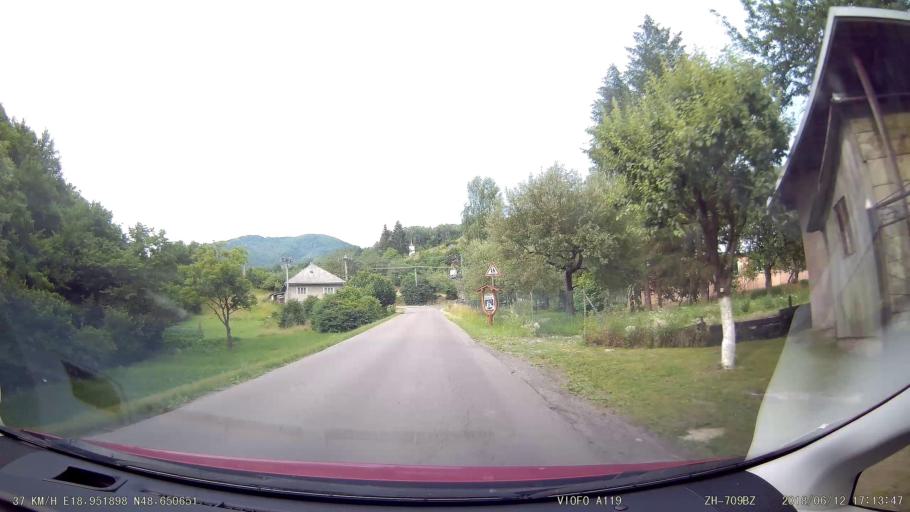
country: SK
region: Banskobystricky
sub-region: Okres Ziar nad Hronom
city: Kremnica
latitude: 48.6508
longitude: 18.9521
